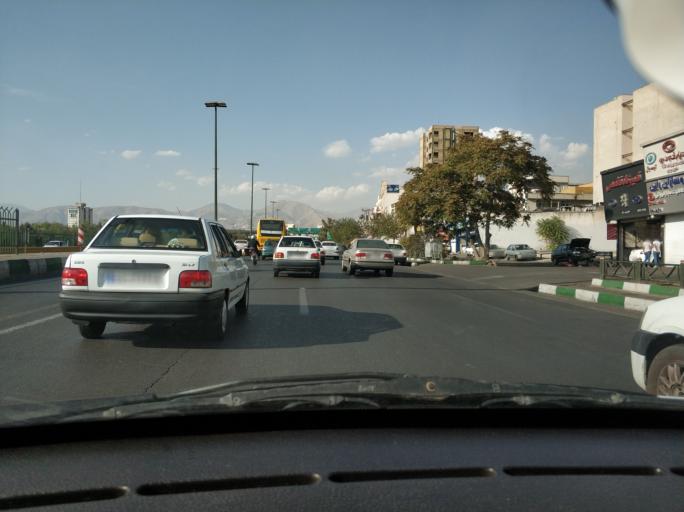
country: IR
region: Tehran
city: Tehran
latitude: 35.7069
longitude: 51.3372
